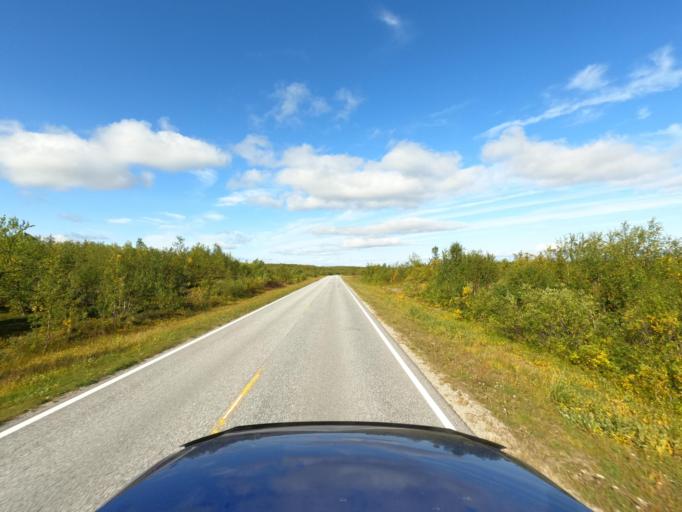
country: NO
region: Finnmark Fylke
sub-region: Karasjok
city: Karasjohka
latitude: 69.5920
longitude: 25.3360
